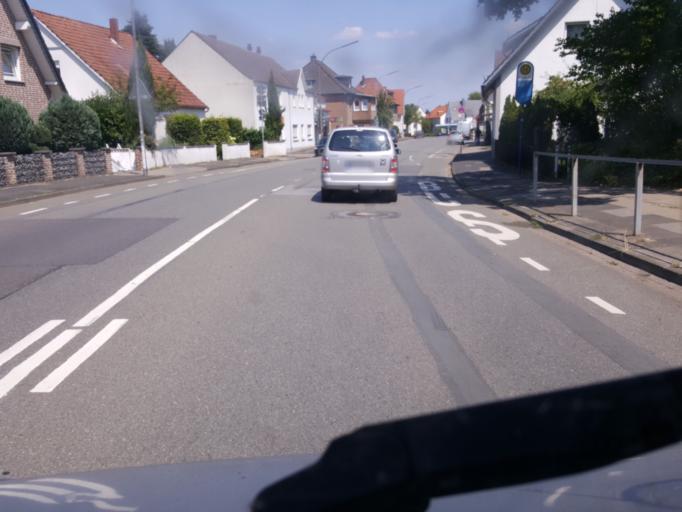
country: DE
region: North Rhine-Westphalia
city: Loehne
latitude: 52.1926
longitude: 8.7148
